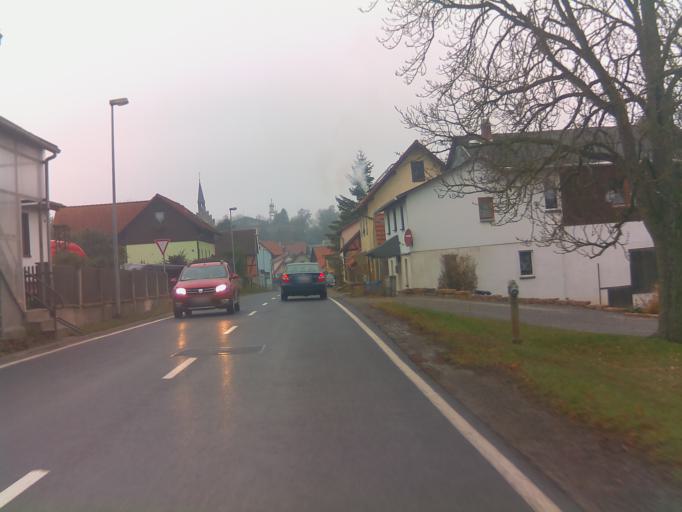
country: DE
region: Thuringia
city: Henfstadt
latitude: 50.4895
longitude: 10.5774
